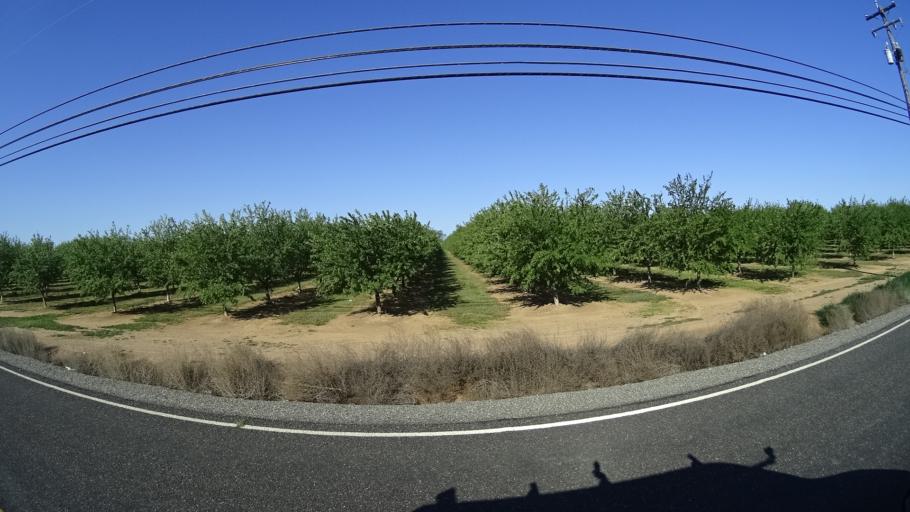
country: US
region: California
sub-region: Glenn County
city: Hamilton City
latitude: 39.7745
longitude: -122.1042
